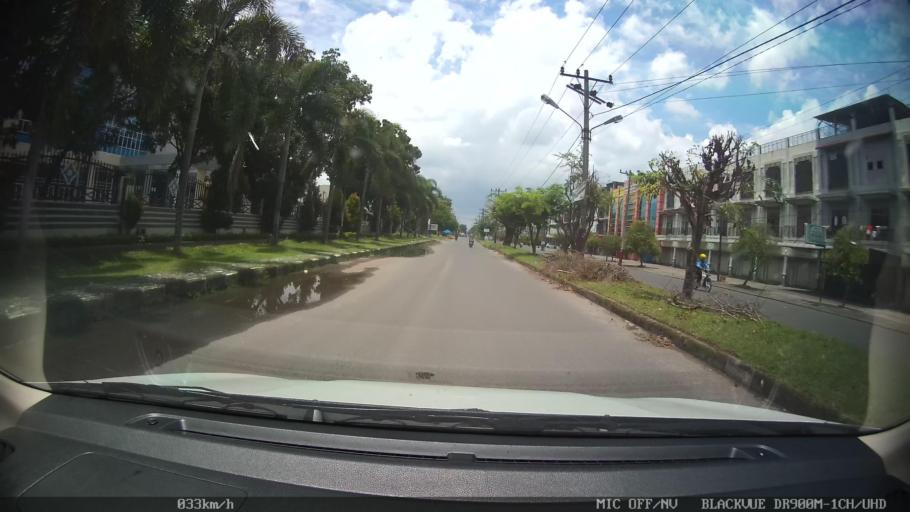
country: ID
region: North Sumatra
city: Medan
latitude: 3.6139
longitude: 98.7178
